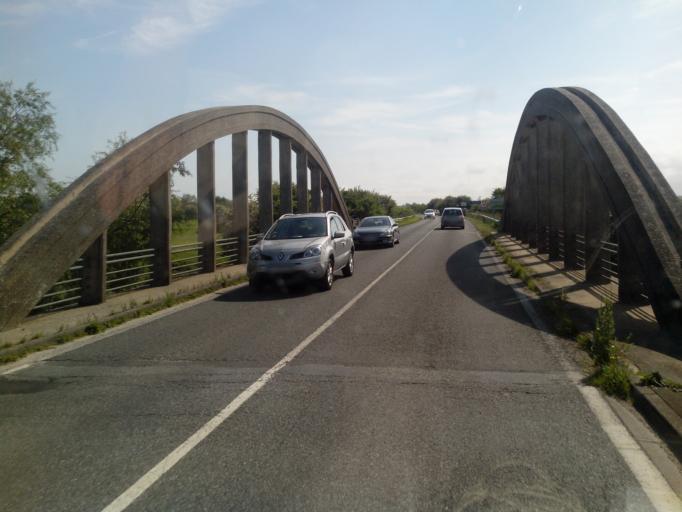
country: FR
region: Picardie
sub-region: Departement de la Somme
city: Quend
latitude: 50.3447
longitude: 1.6455
